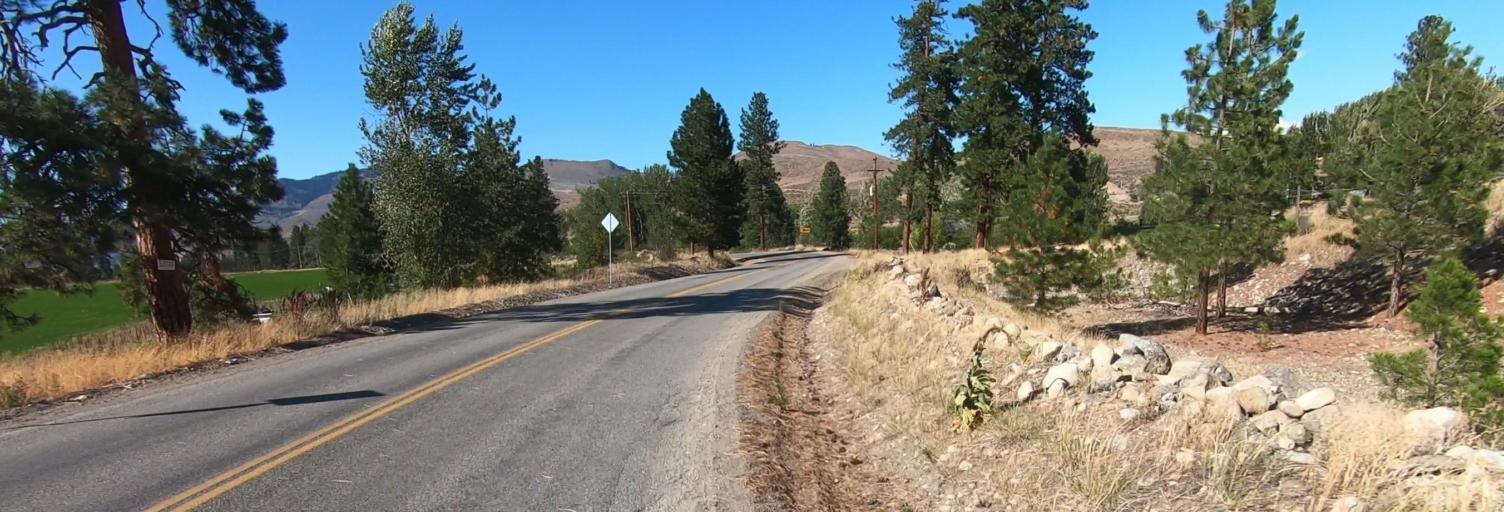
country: US
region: Washington
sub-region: Okanogan County
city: Brewster
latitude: 48.4801
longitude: -120.2214
